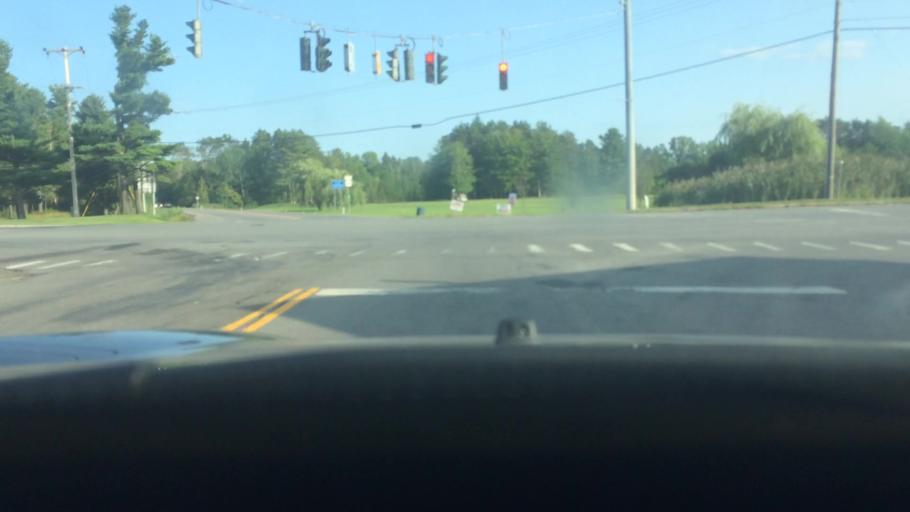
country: US
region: New York
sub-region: St. Lawrence County
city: Canton
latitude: 44.5976
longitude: -75.1477
